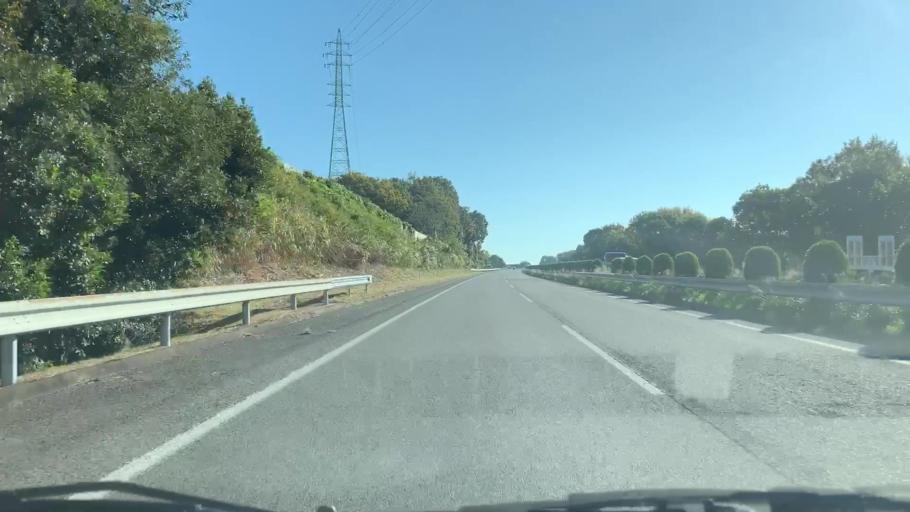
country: JP
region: Saga Prefecture
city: Takeocho-takeo
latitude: 33.2881
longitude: 130.1438
